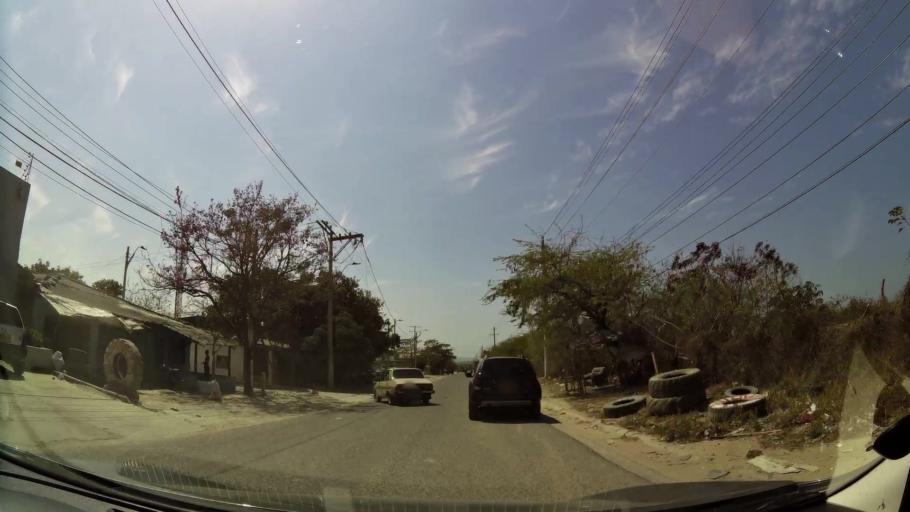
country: CO
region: Atlantico
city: Barranquilla
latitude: 10.9818
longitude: -74.8398
